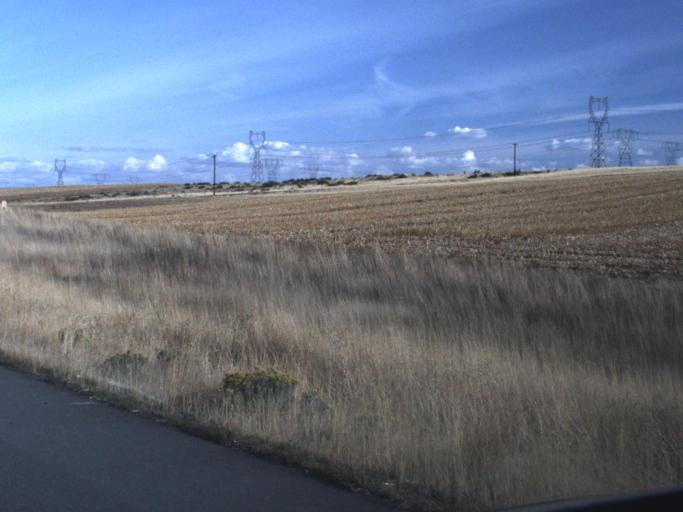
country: US
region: Oregon
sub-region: Morrow County
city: Irrigon
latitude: 45.9464
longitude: -119.4689
